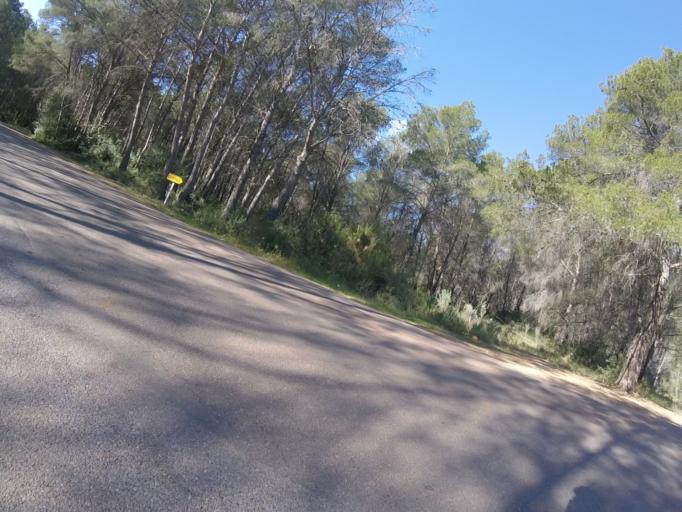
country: ES
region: Valencia
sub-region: Provincia de Castello
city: Orpesa/Oropesa del Mar
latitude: 40.0810
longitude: 0.1221
